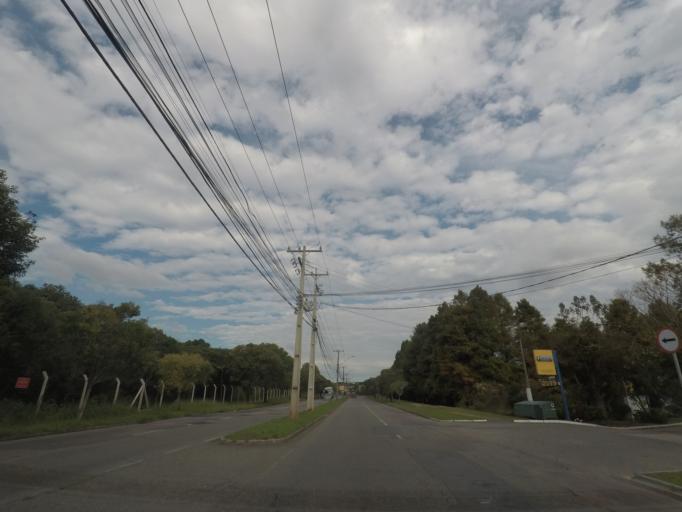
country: BR
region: Parana
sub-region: Curitiba
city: Curitiba
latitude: -25.5240
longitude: -49.3171
